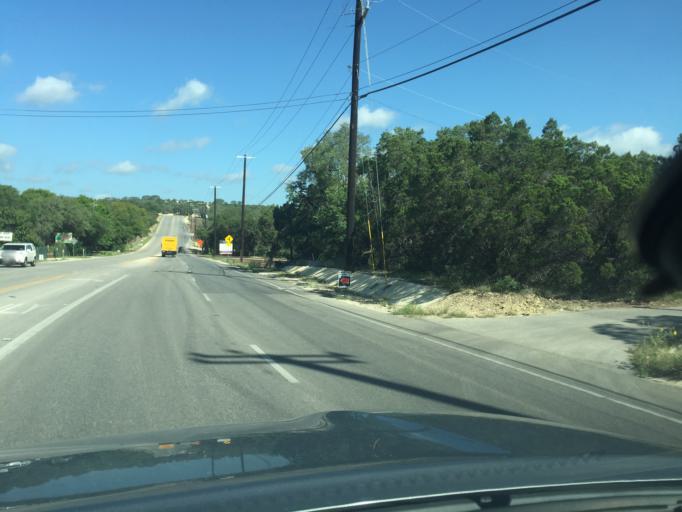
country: US
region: Texas
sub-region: Bexar County
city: Timberwood Park
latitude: 29.7127
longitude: -98.4665
